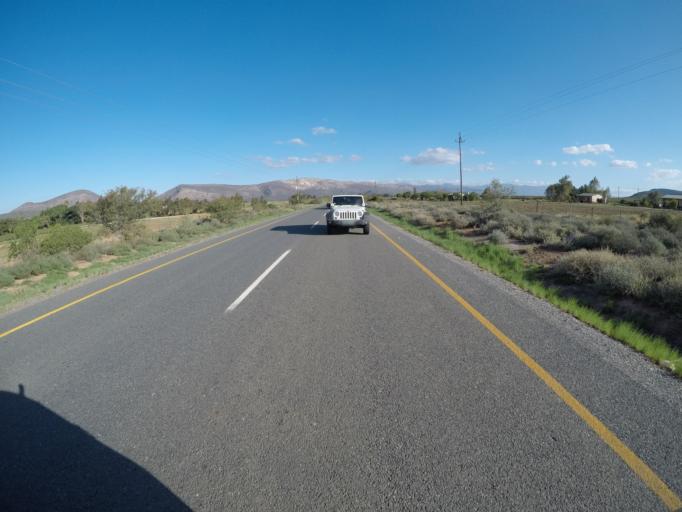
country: ZA
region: Western Cape
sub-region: Cape Winelands District Municipality
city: Ashton
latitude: -33.8006
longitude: 19.7815
